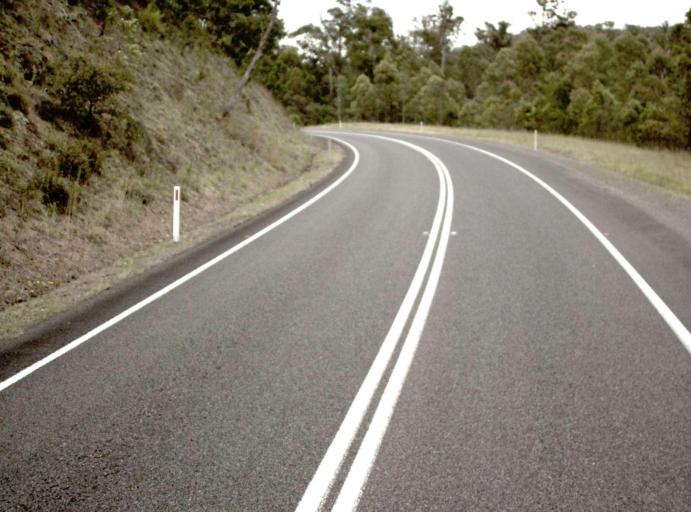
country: AU
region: New South Wales
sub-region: Bombala
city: Bombala
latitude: -37.2576
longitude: 149.2400
